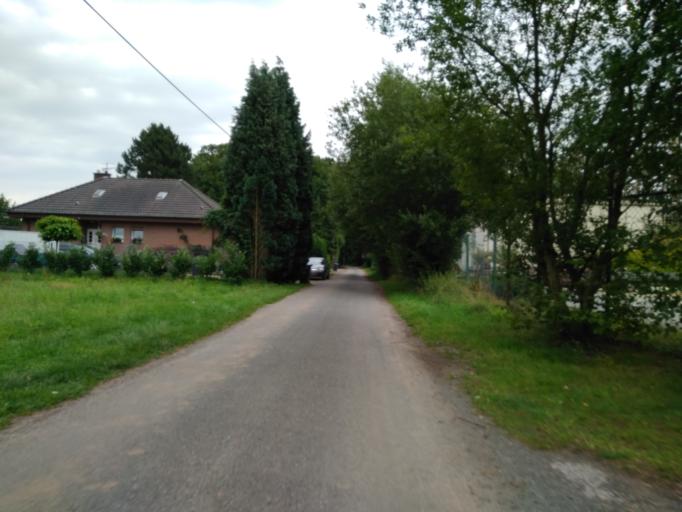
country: DE
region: North Rhine-Westphalia
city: Dorsten
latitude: 51.6254
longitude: 6.9752
